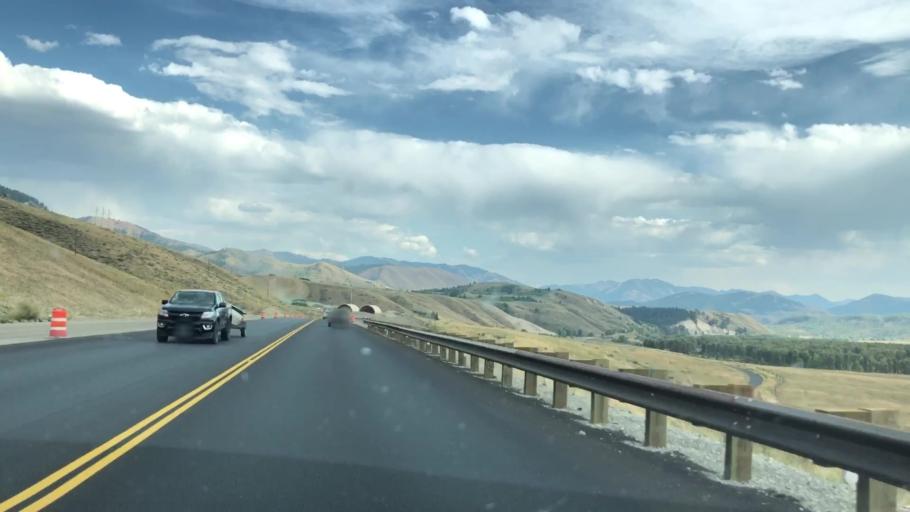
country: US
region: Wyoming
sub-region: Teton County
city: South Park
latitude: 43.4075
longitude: -110.7640
